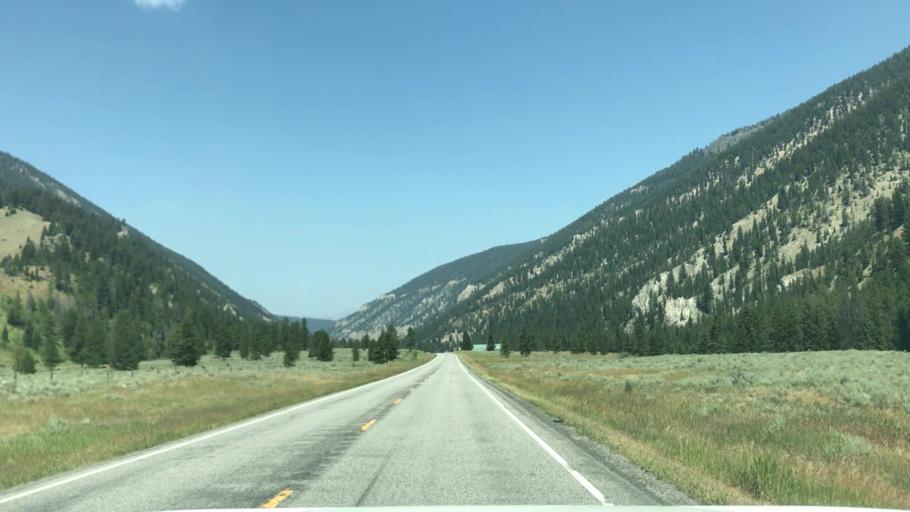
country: US
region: Montana
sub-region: Gallatin County
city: Big Sky
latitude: 45.1099
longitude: -111.2235
